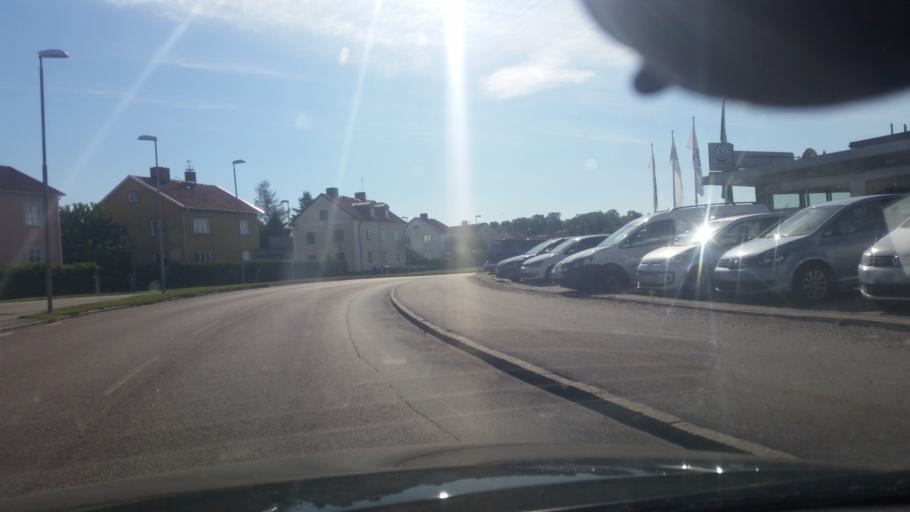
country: SE
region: Soedermanland
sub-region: Nykopings Kommun
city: Nykoping
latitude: 58.7516
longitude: 16.9937
